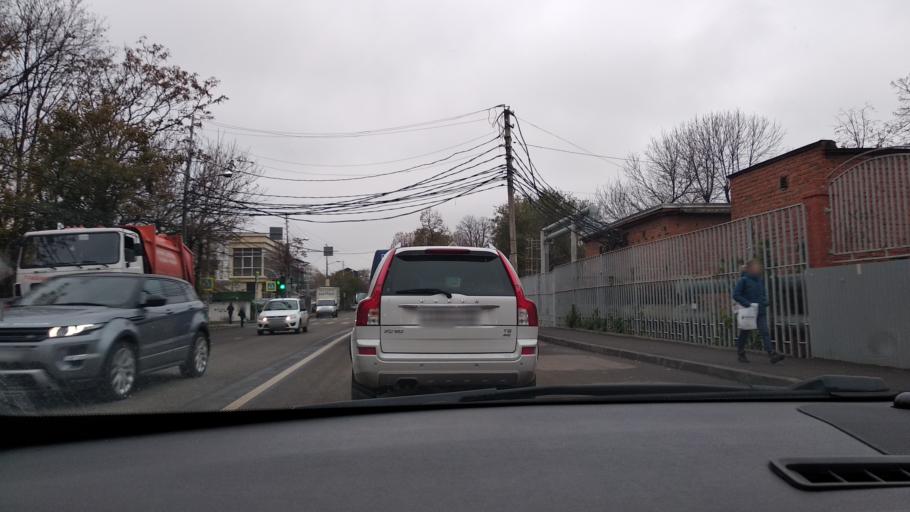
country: RU
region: Krasnodarskiy
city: Krasnodar
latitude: 45.0414
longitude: 38.9858
